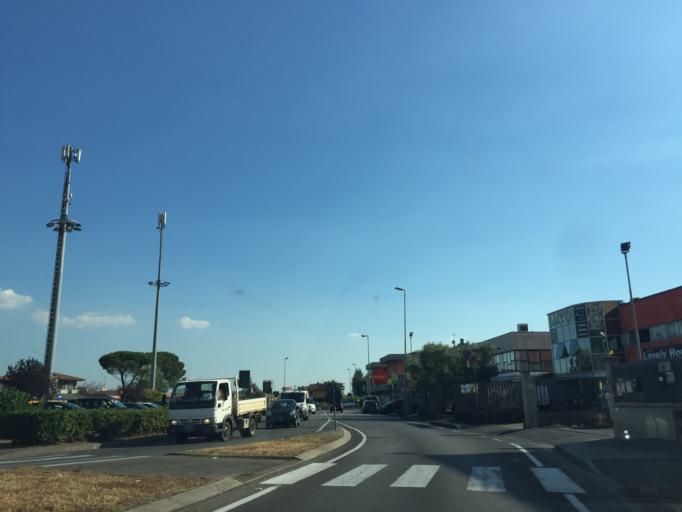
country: IT
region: Tuscany
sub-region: Provincia di Pistoia
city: Monsummano Terme
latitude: 43.8671
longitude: 10.8087
